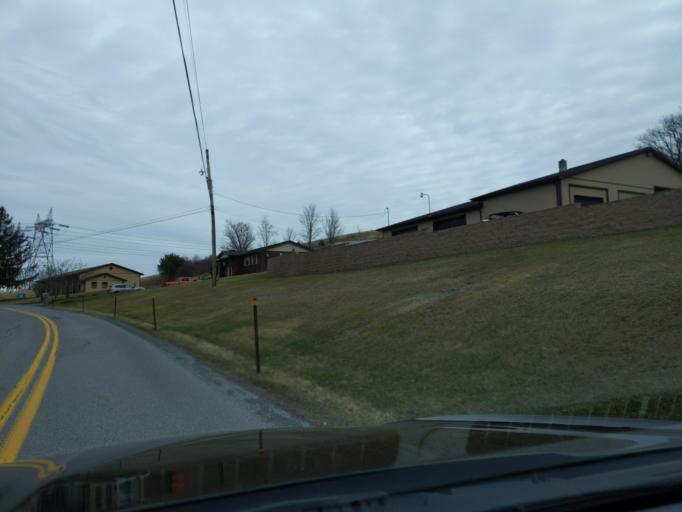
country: US
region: Pennsylvania
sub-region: Blair County
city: Greenwood
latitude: 40.5820
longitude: -78.3790
